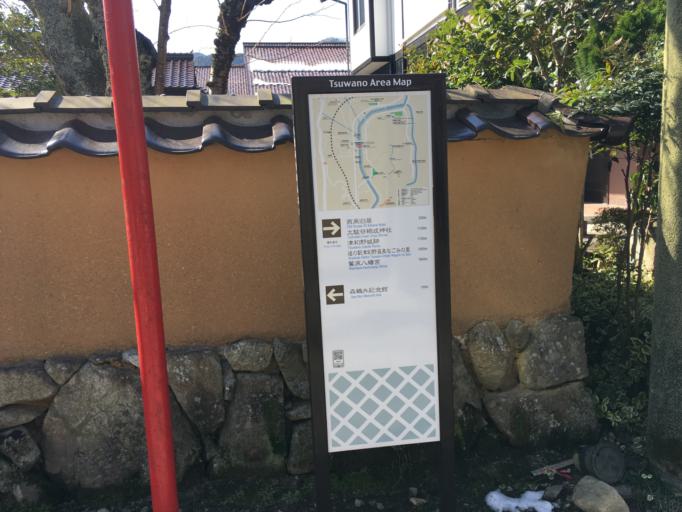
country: JP
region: Shimane
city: Masuda
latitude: 34.4579
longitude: 131.7688
